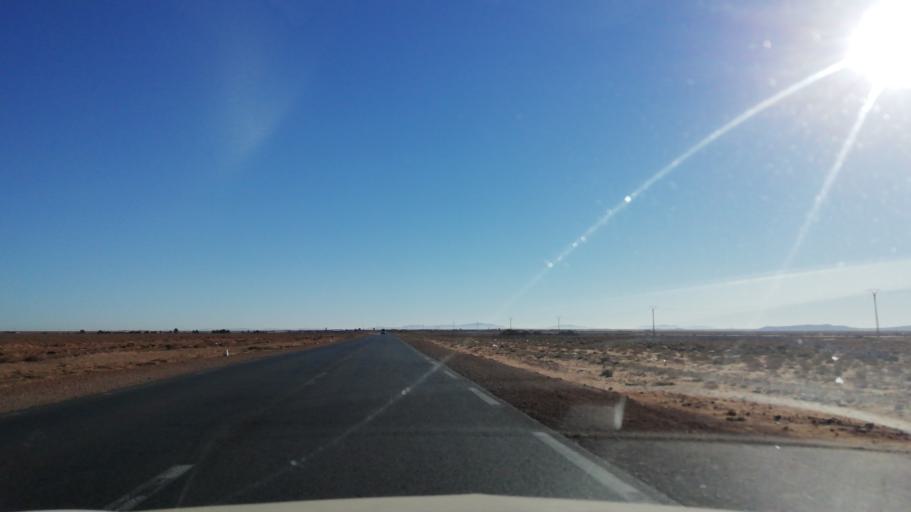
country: DZ
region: El Bayadh
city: El Bayadh
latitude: 33.8553
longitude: 0.5999
